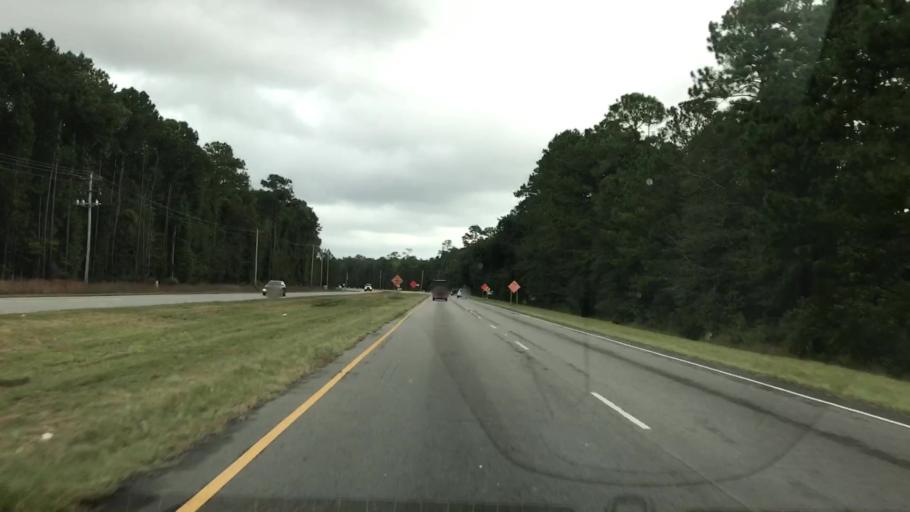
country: US
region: South Carolina
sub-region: Beaufort County
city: Bluffton
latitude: 32.3282
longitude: -80.9301
